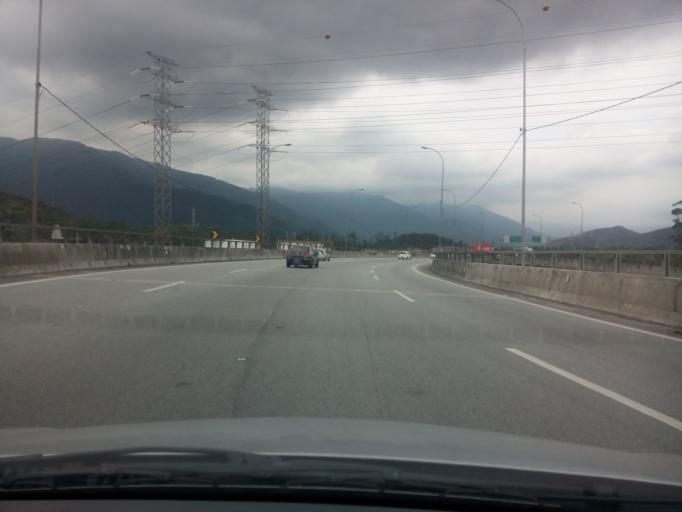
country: BR
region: Sao Paulo
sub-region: Cubatao
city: Cubatao
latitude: -23.8920
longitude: -46.4359
